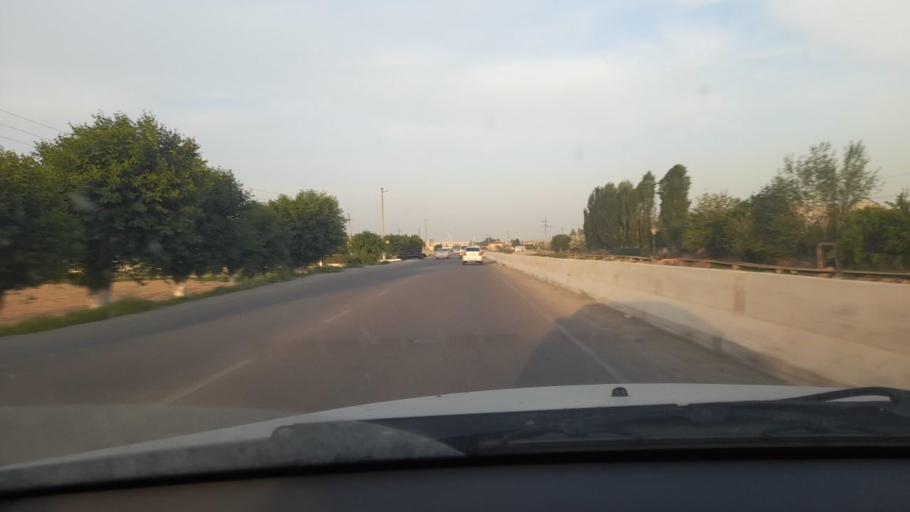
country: UZ
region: Sirdaryo
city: Guliston
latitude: 40.5074
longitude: 68.7453
